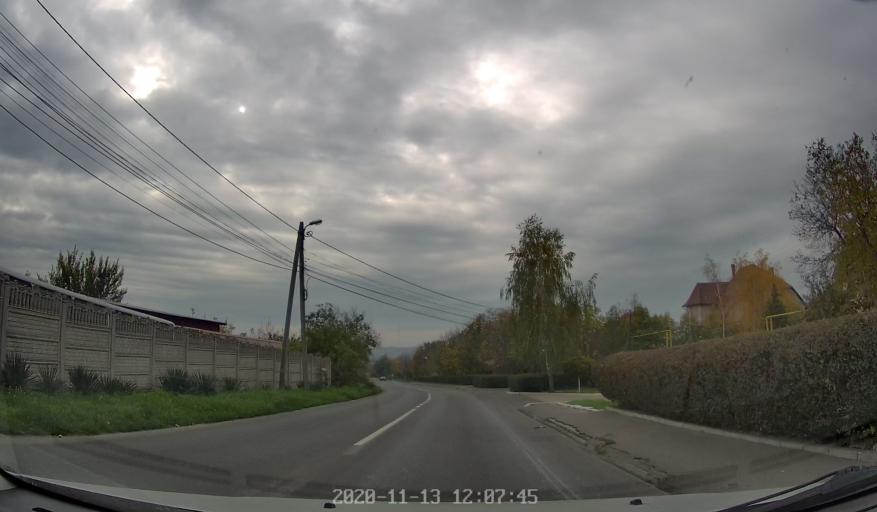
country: MD
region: Chisinau
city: Chisinau
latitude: 46.9718
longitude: 28.8339
